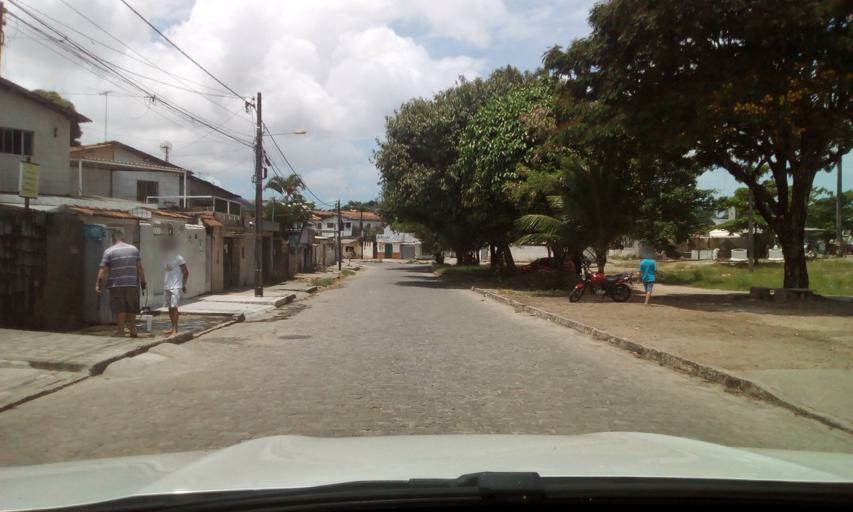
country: BR
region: Paraiba
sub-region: Joao Pessoa
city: Joao Pessoa
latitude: -7.1728
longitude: -34.8877
